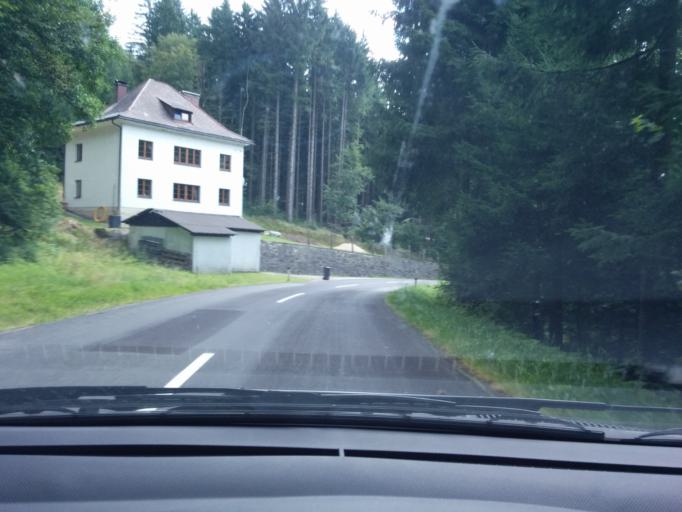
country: AT
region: Upper Austria
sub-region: Politischer Bezirk Rohrbach
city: Ulrichsberg
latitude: 48.7194
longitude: 13.8973
